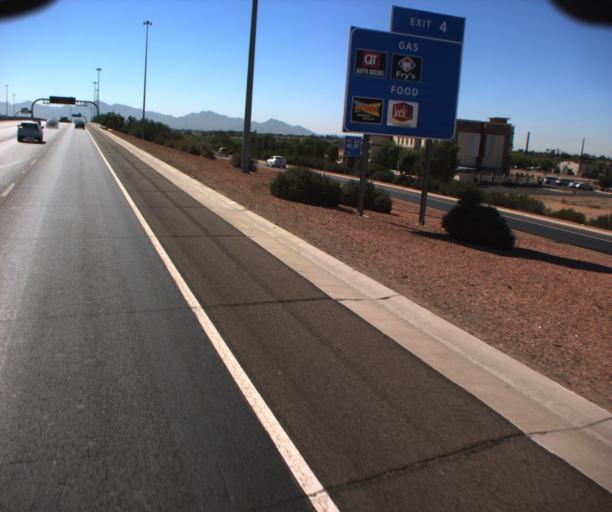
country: US
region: Arizona
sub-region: Maricopa County
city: Tolleson
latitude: 33.5114
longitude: -112.2693
